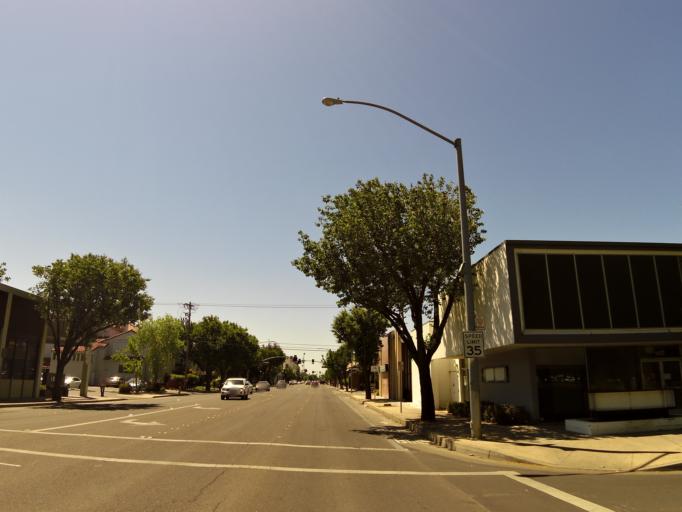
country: US
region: California
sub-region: Merced County
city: Merced
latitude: 37.3051
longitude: -120.4832
